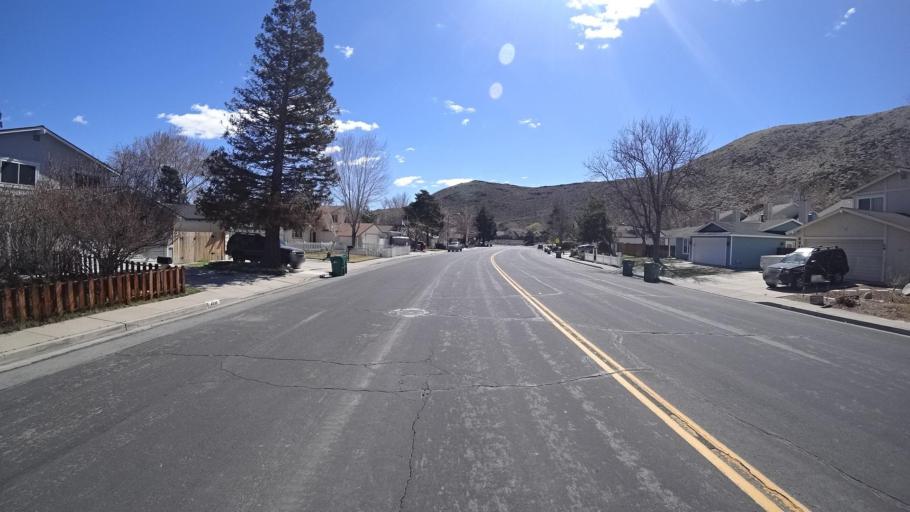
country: US
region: Nevada
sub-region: Washoe County
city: Sparks
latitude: 39.4774
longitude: -119.7542
